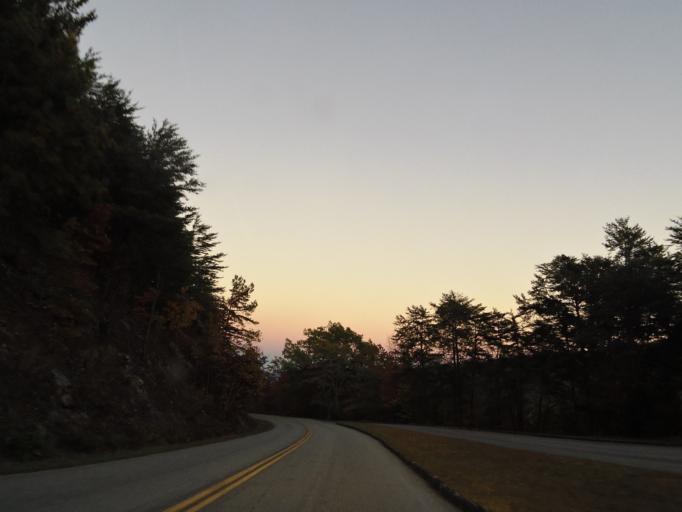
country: US
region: Tennessee
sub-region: Blount County
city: Maryville
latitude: 35.6728
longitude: -83.8996
